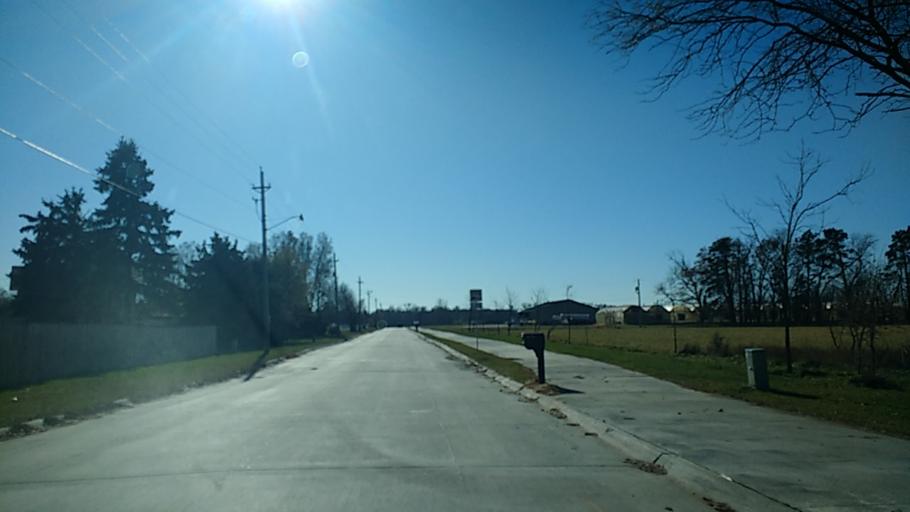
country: US
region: South Dakota
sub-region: Union County
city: North Sioux City
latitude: 42.5461
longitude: -96.5268
